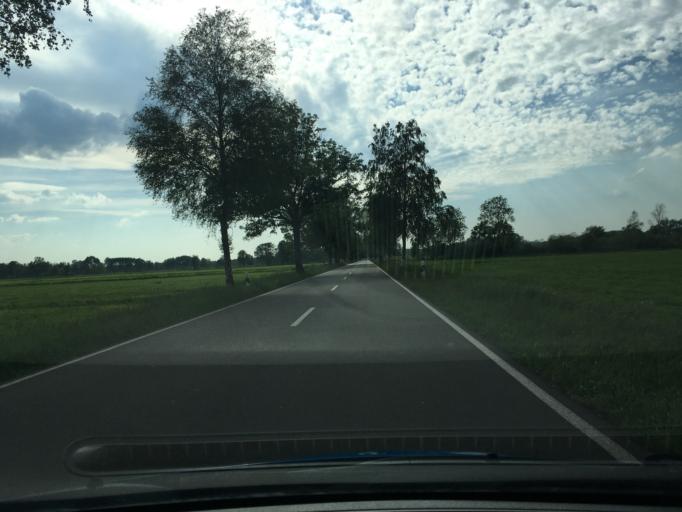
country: DE
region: Lower Saxony
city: Kalbe
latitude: 53.2790
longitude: 9.5986
